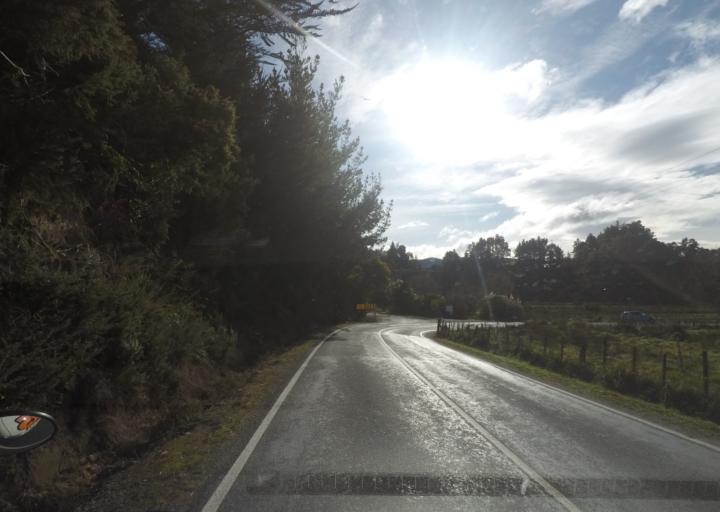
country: NZ
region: Tasman
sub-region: Tasman District
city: Motueka
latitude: -41.0175
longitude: 172.9812
